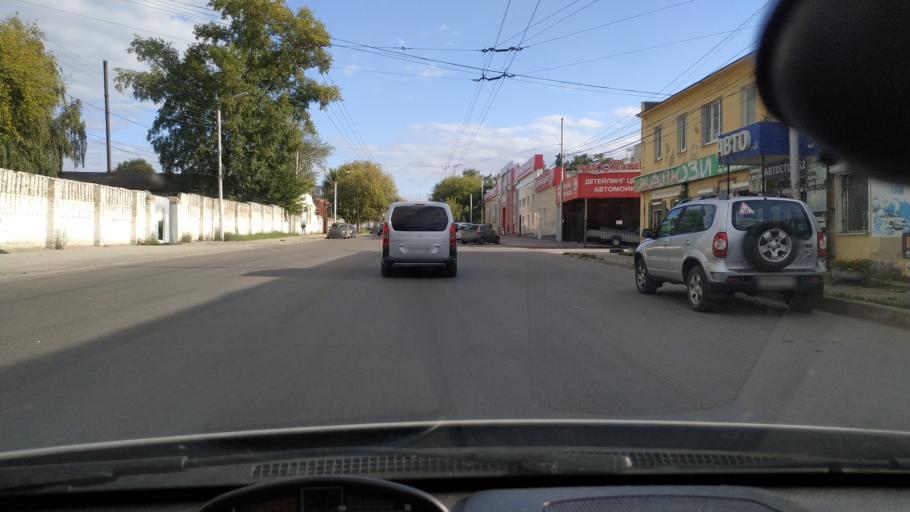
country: RU
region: Rjazan
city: Ryazan'
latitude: 54.6150
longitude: 39.6943
